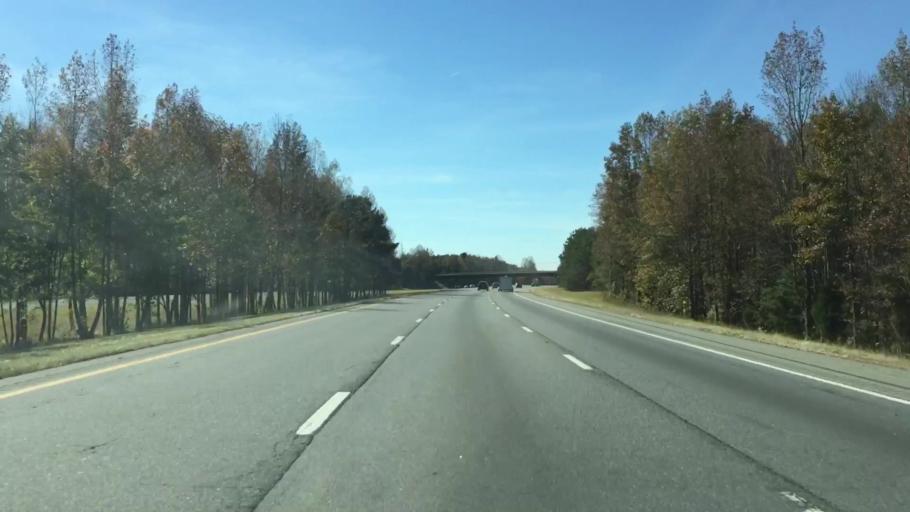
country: US
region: North Carolina
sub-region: Davidson County
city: Lexington
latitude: 35.7773
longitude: -80.2729
